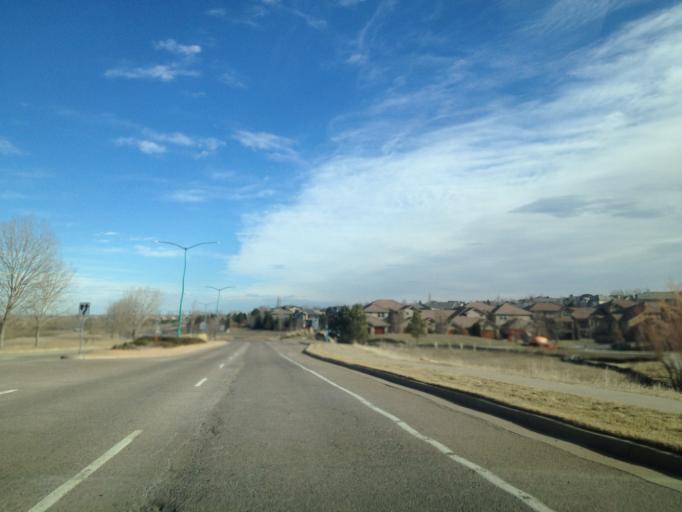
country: US
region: Colorado
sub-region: Boulder County
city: Superior
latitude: 39.9287
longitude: -105.1642
